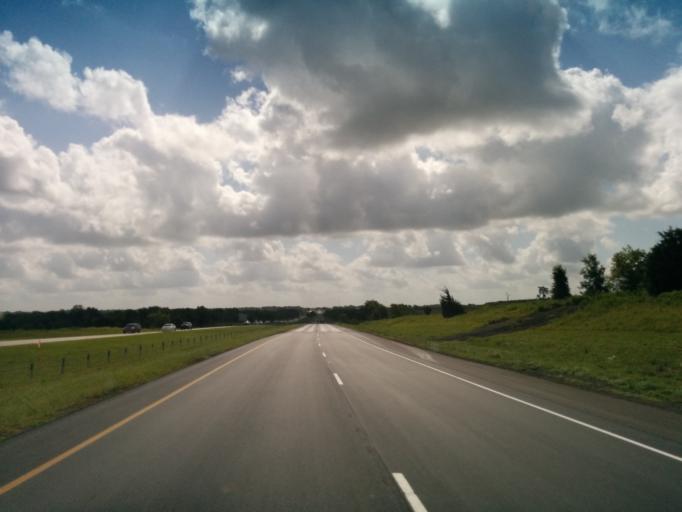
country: US
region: Texas
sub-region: Fayette County
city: Schulenburg
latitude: 29.6958
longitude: -96.8856
